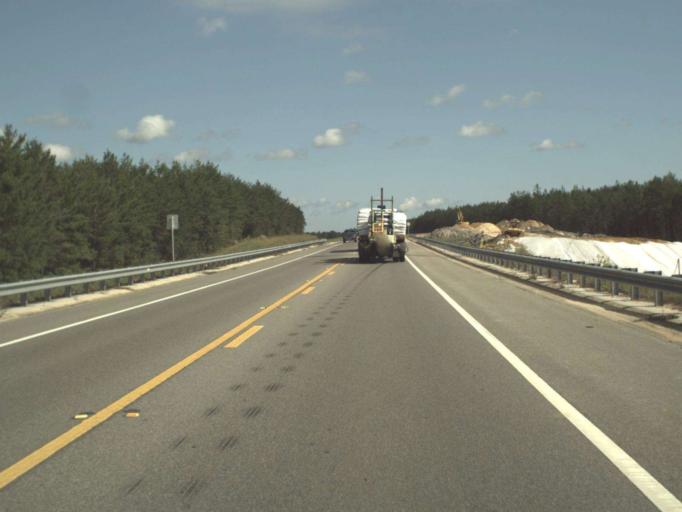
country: US
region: Florida
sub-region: Walton County
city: Freeport
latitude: 30.5150
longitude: -86.1109
